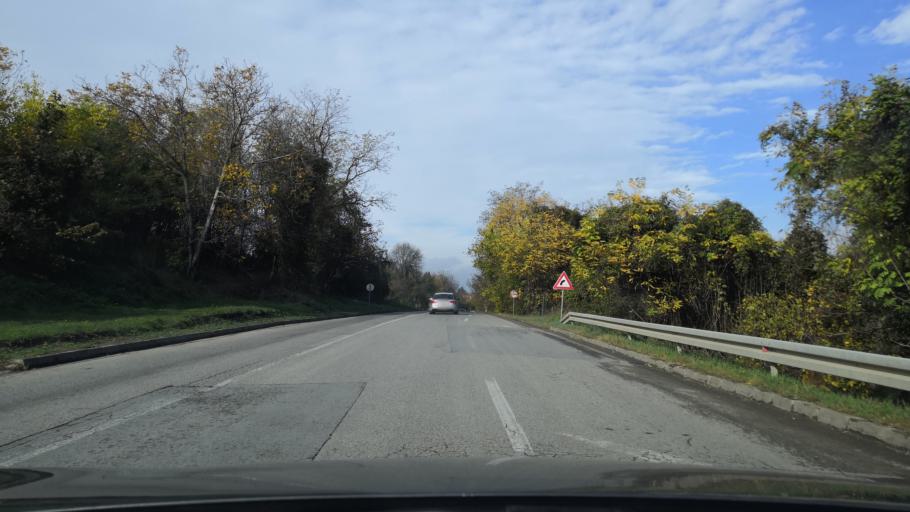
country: RS
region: Autonomna Pokrajina Vojvodina
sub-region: Juznobacki Okrug
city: Sremski Karlovci
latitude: 45.2196
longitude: 19.9047
